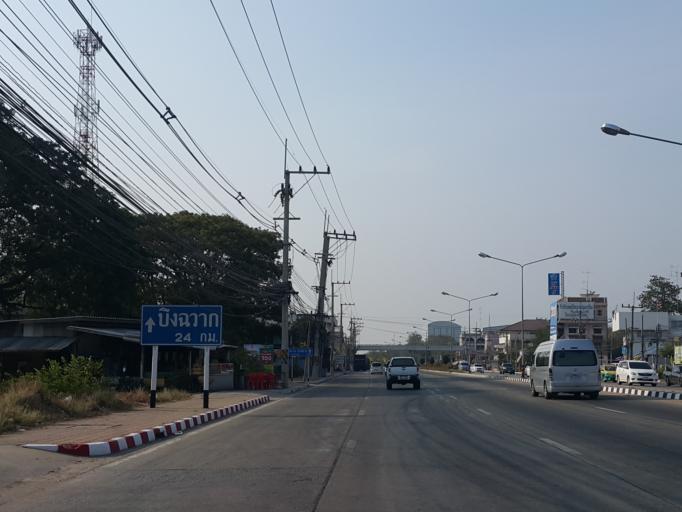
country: TH
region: Suphan Buri
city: Sam Chuk
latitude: 14.7525
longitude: 100.0973
